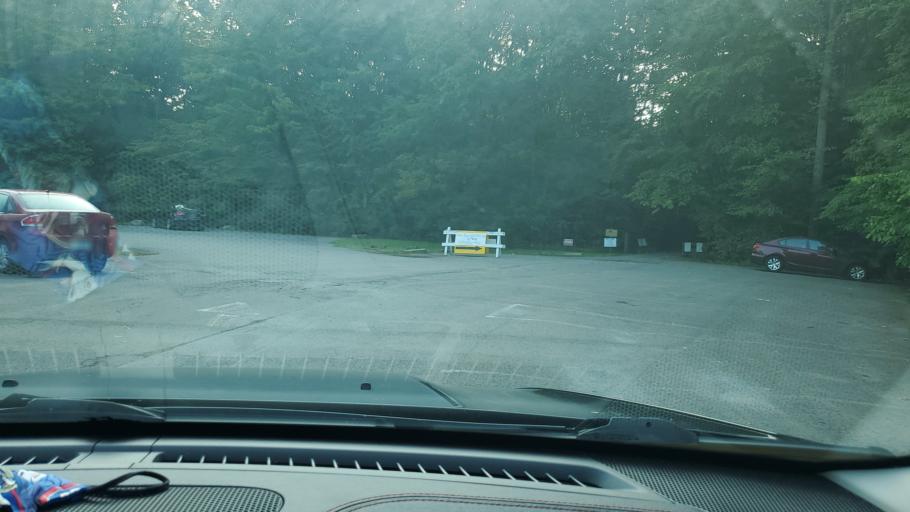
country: US
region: Ohio
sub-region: Mahoning County
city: Boardman
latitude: 41.0179
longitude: -80.6499
